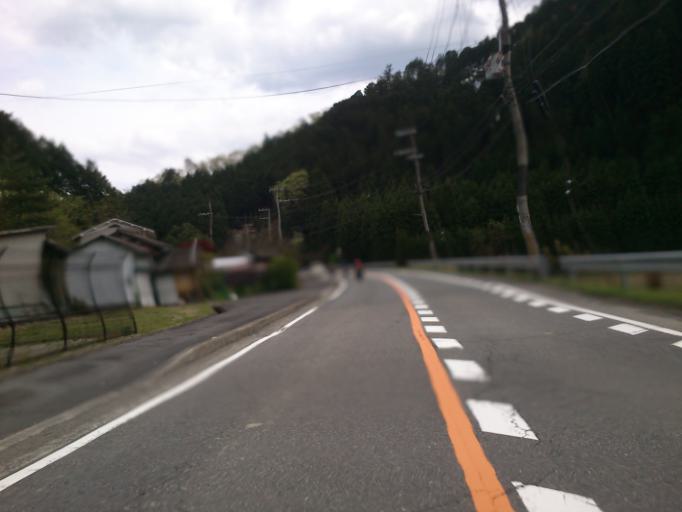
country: JP
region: Kyoto
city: Kameoka
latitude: 35.2124
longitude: 135.5641
